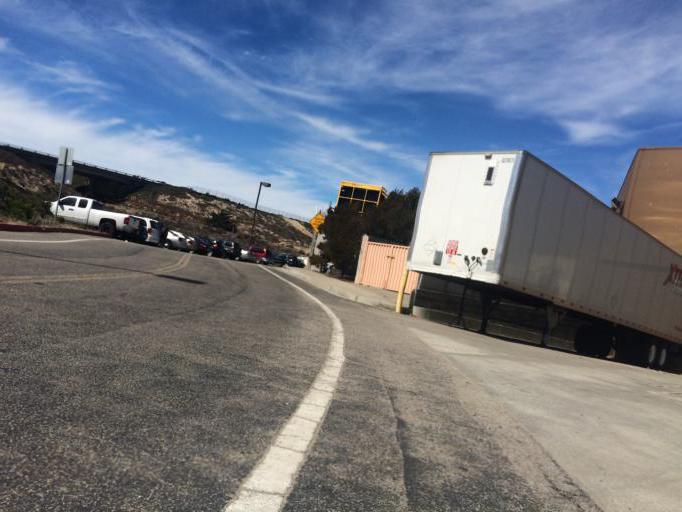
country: US
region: California
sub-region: Monterey County
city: Seaside
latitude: 36.6190
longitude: -121.8462
